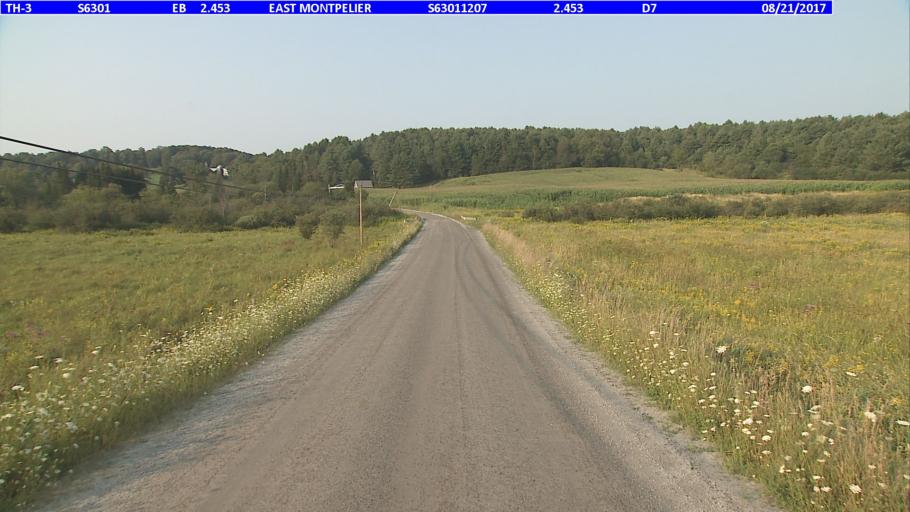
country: US
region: Vermont
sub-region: Washington County
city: Montpelier
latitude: 44.2935
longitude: -72.5186
